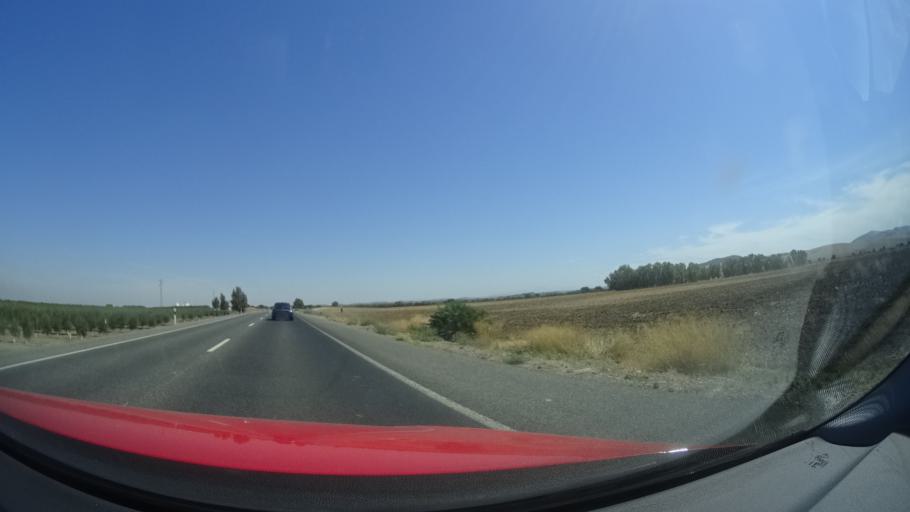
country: ES
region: Andalusia
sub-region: Provincia de Sevilla
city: Las Cabezas de San Juan
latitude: 36.9044
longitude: -5.9791
